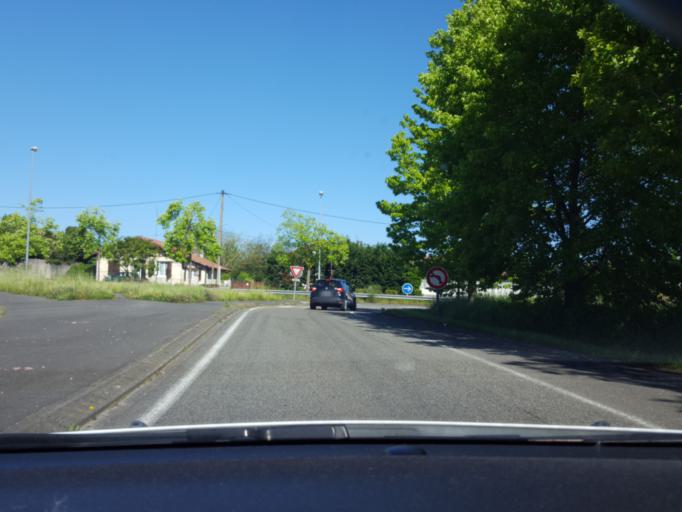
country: FR
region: Aquitaine
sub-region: Departement des Landes
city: Tarnos
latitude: 43.5528
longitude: -1.4572
